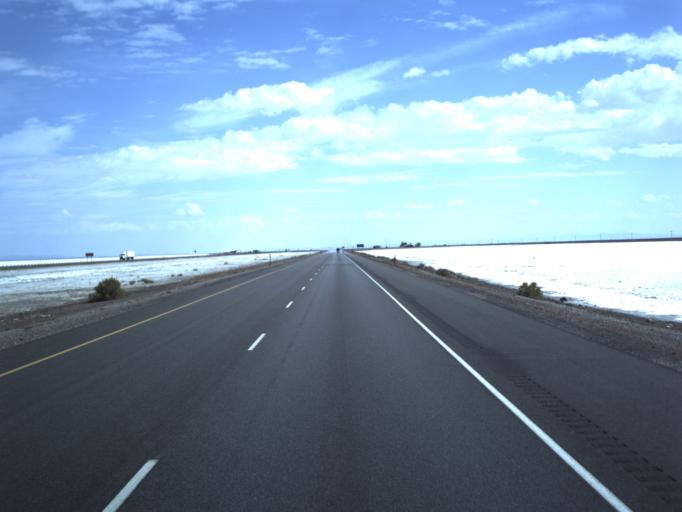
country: US
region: Utah
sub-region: Tooele County
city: Wendover
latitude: 40.7389
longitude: -113.8746
